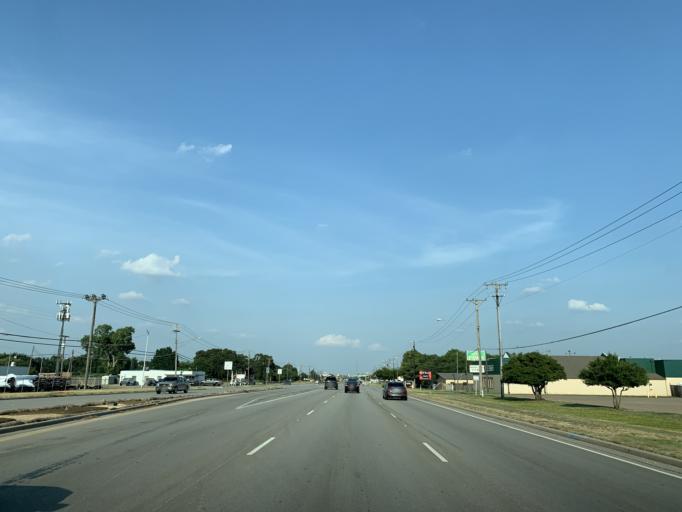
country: US
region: Texas
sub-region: Tarrant County
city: Hurst
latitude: 32.8089
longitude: -97.1740
